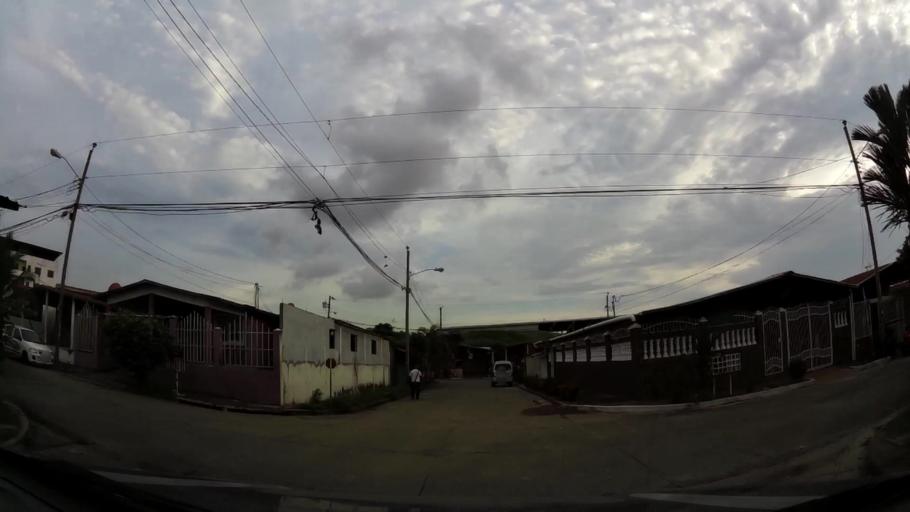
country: PA
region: Panama
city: Tocumen
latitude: 9.0942
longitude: -79.3957
